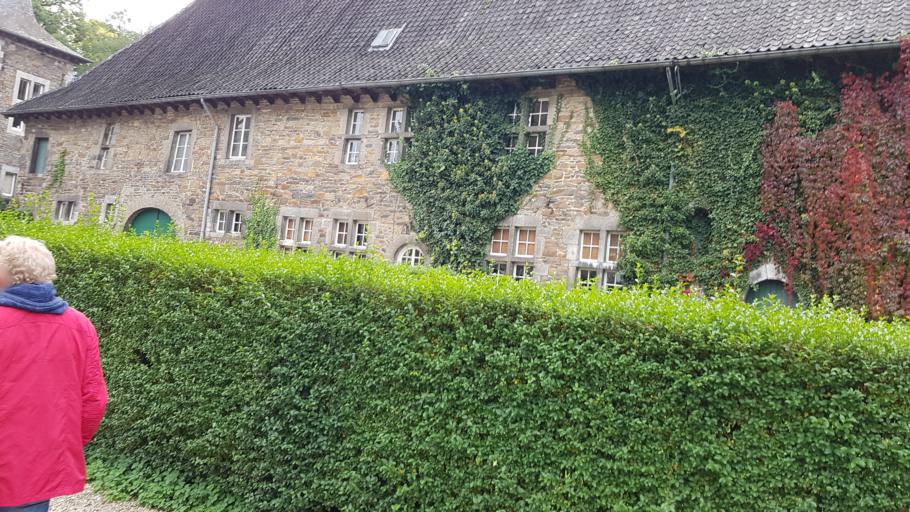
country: BE
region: Flanders
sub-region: Provincie Limburg
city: Sint-Pieters-Voeren
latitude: 50.6980
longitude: 5.8047
